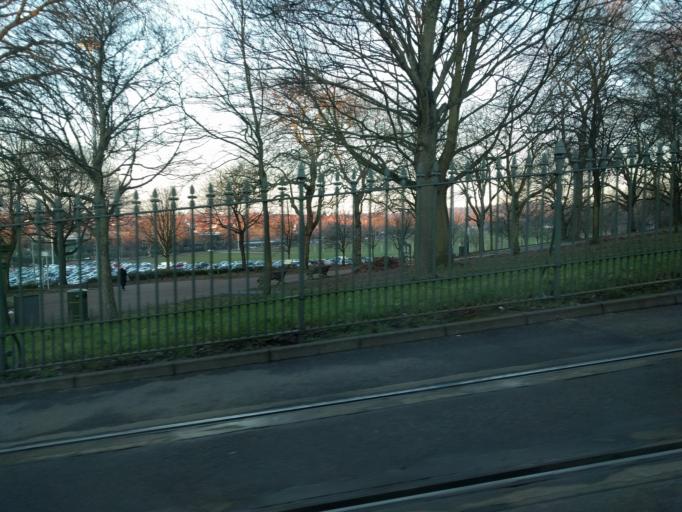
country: GB
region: England
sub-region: Nottingham
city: Nottingham
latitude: 52.9641
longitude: -1.1661
